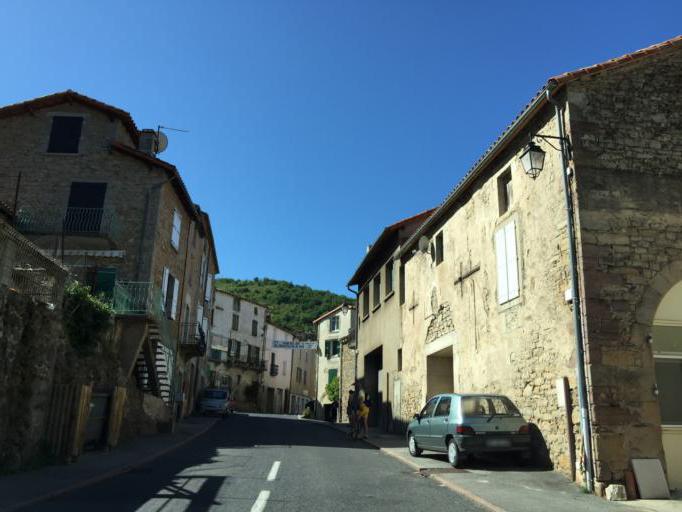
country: FR
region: Midi-Pyrenees
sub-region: Departement de l'Aveyron
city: Saint-Georges-de-Luzencon
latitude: 44.0499
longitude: 2.8982
